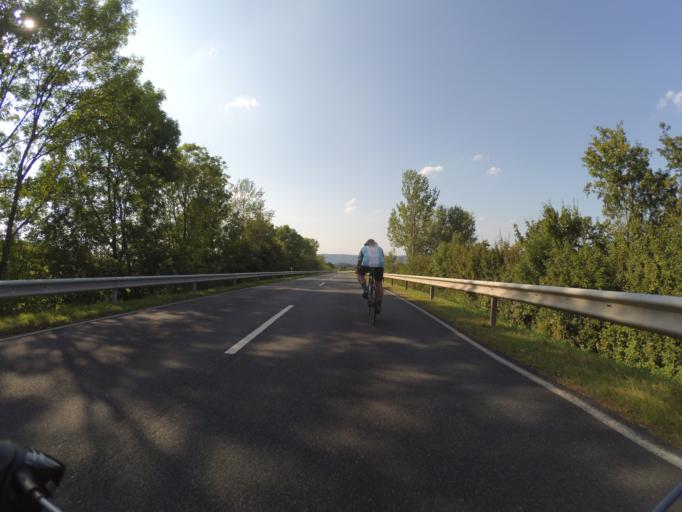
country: DE
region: Rheinland-Pfalz
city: Minheim
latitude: 49.8543
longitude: 6.9623
